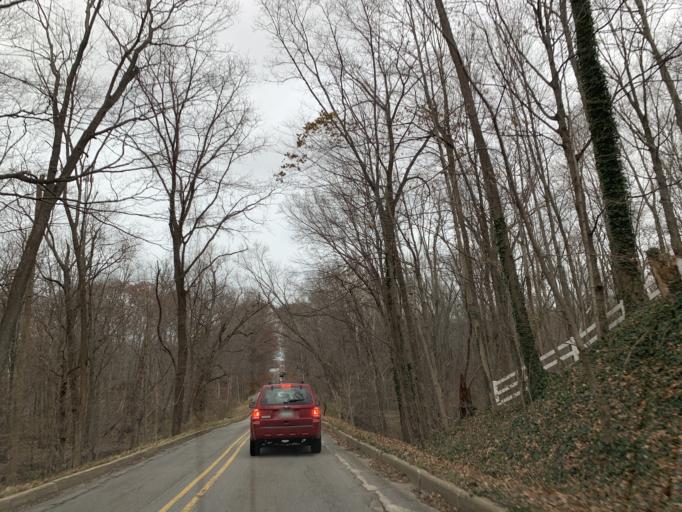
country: US
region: Michigan
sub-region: Berrien County
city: Three Oaks
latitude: 41.8238
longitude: -86.6683
